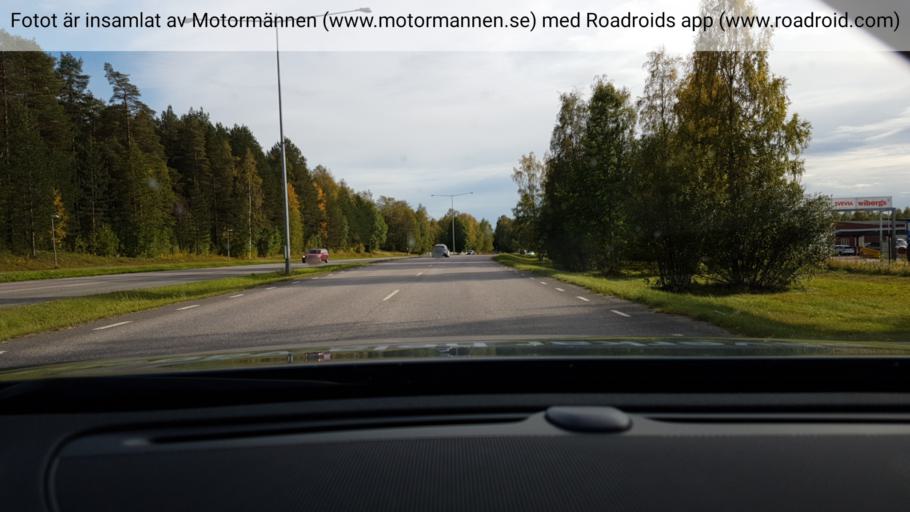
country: SE
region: Norrbotten
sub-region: Lulea Kommun
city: Lulea
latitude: 65.6086
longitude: 22.1371
